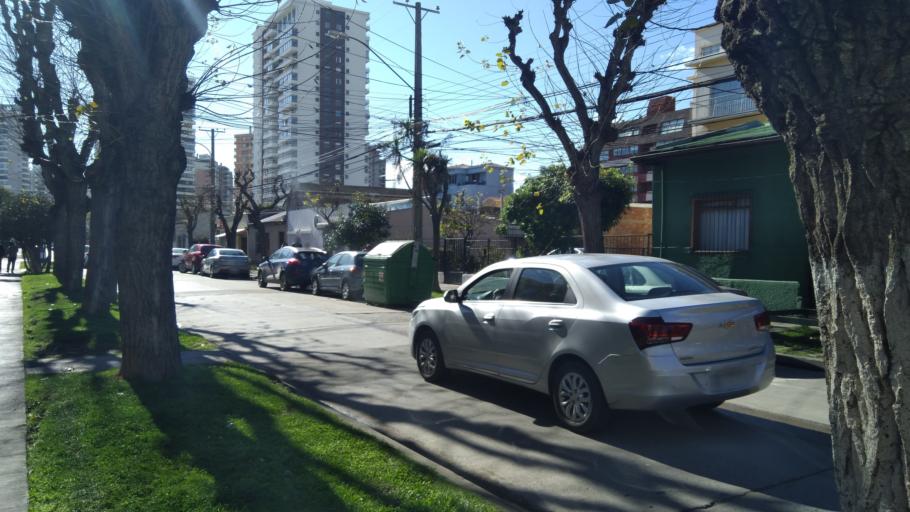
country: CL
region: Valparaiso
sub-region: Provincia de Valparaiso
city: Vina del Mar
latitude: -33.0175
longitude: -71.5556
